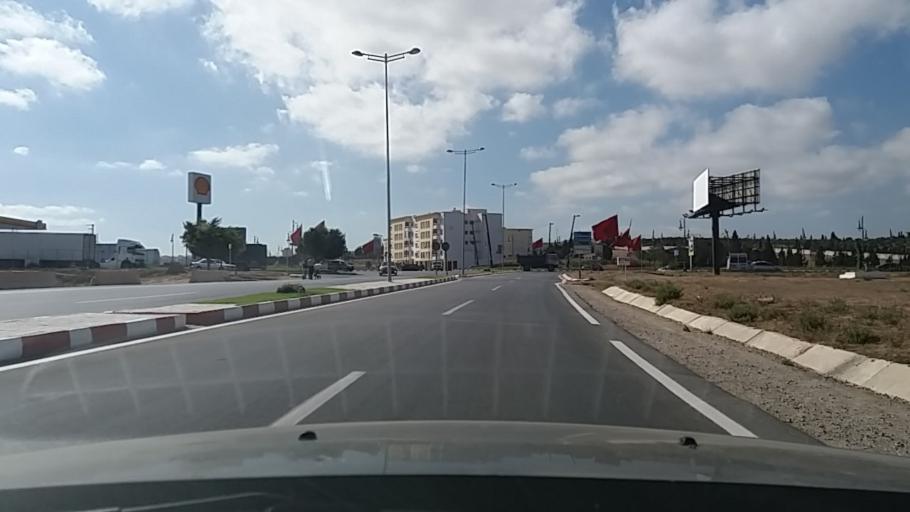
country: MA
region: Tanger-Tetouan
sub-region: Tanger-Assilah
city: Boukhalef
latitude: 35.7258
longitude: -5.8952
